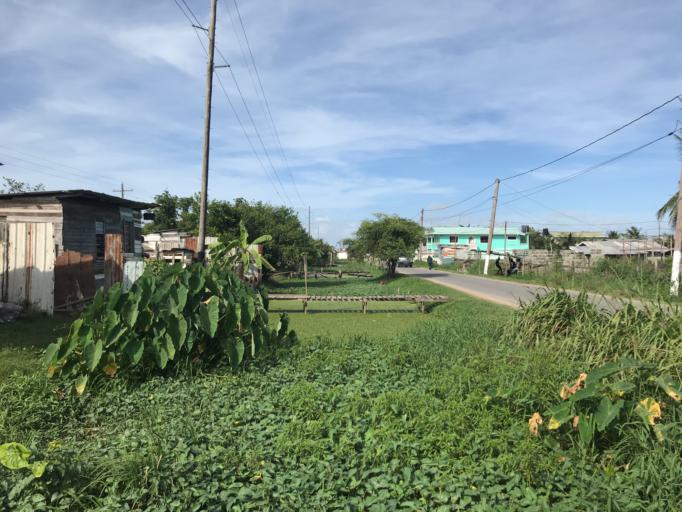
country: GY
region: Demerara-Mahaica
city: Georgetown
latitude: 6.8005
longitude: -58.1277
